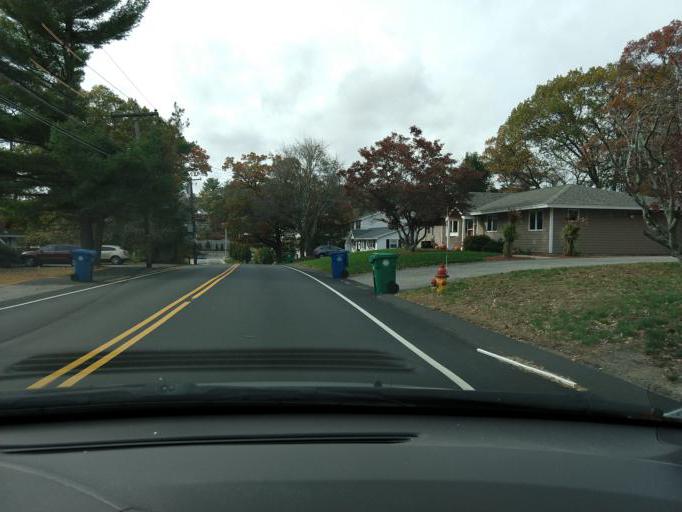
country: US
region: Massachusetts
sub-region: Middlesex County
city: Burlington
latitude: 42.5139
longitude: -71.2002
